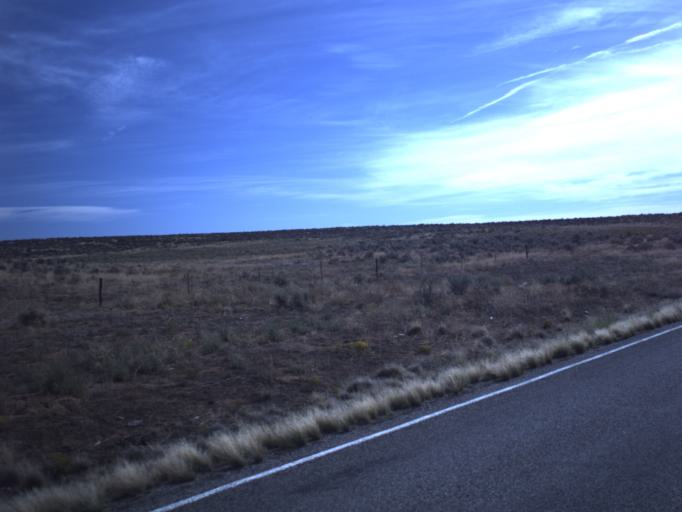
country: US
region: Utah
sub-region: San Juan County
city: Blanding
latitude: 37.4272
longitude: -109.3530
